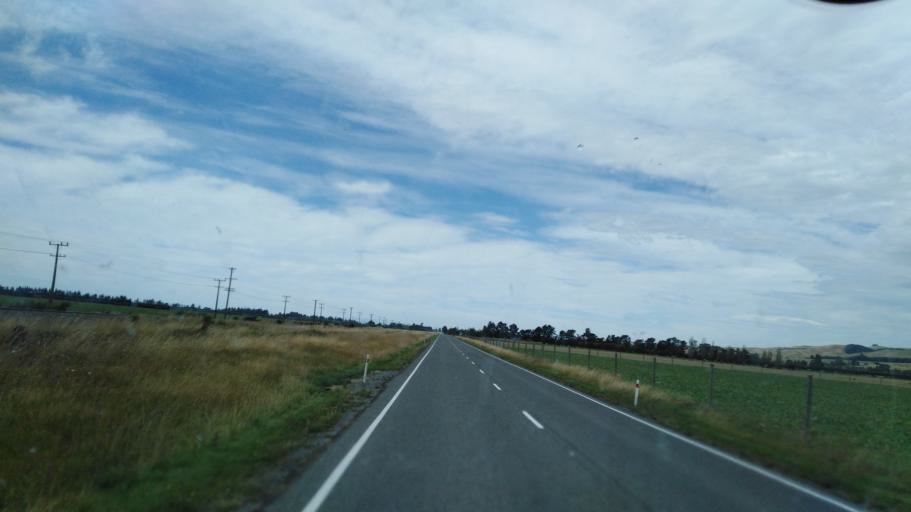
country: NZ
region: Canterbury
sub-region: Selwyn District
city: Darfield
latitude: -43.3607
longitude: 171.9703
